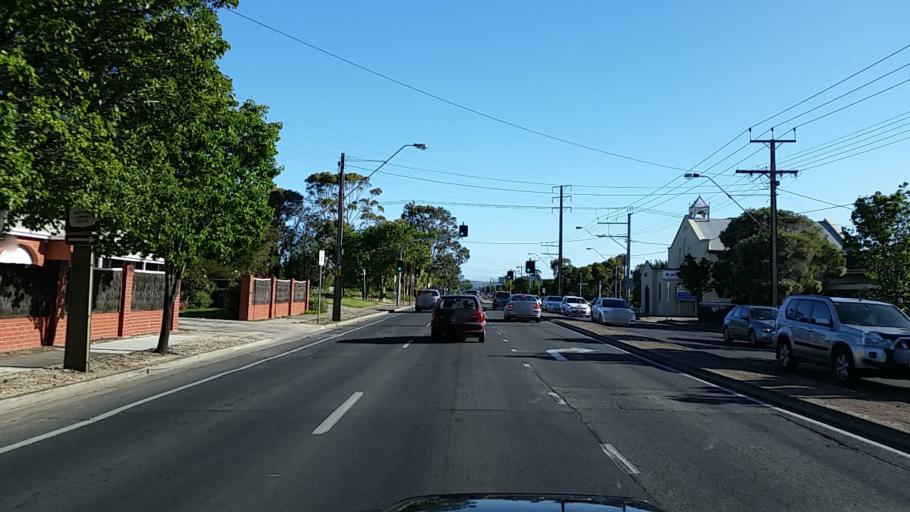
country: AU
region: South Australia
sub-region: City of West Torrens
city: Plympton
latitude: -34.9589
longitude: 138.5544
